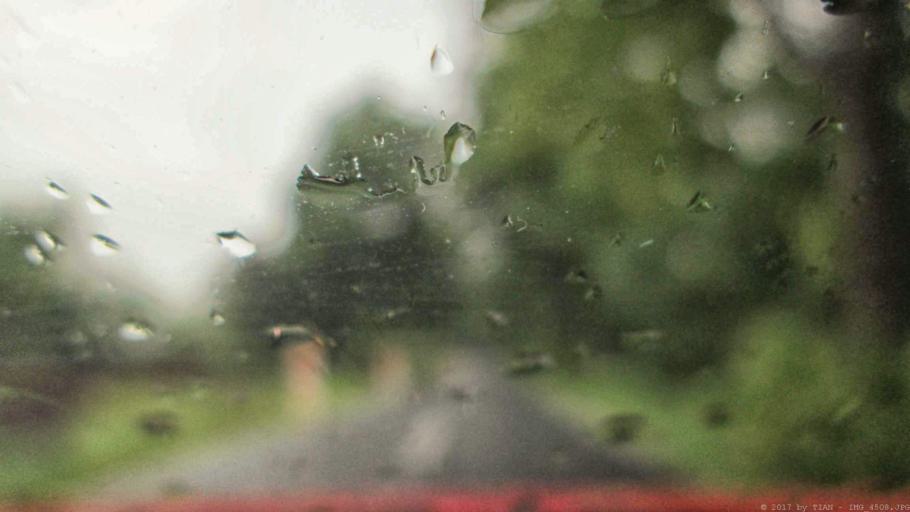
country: DE
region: Lower Saxony
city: Jembke
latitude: 52.4783
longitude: 10.7839
